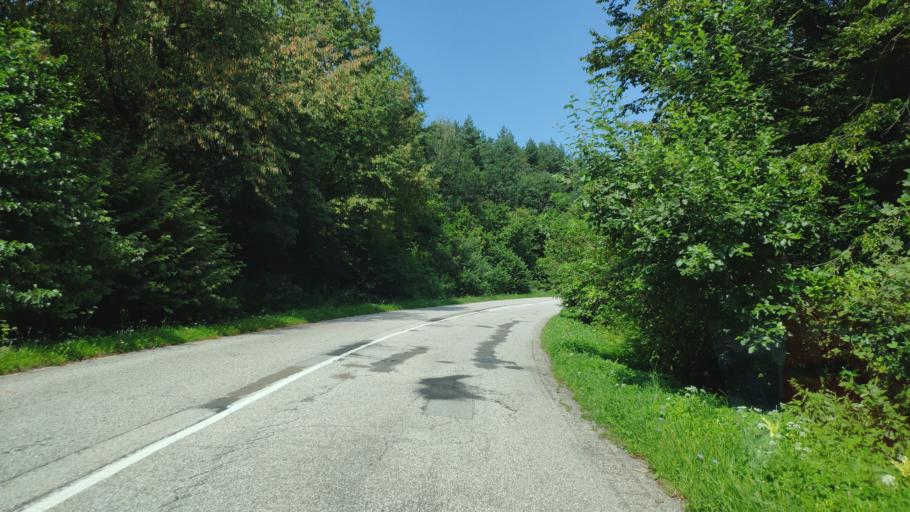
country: SK
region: Kosicky
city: Dobsina
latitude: 48.7156
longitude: 20.4020
